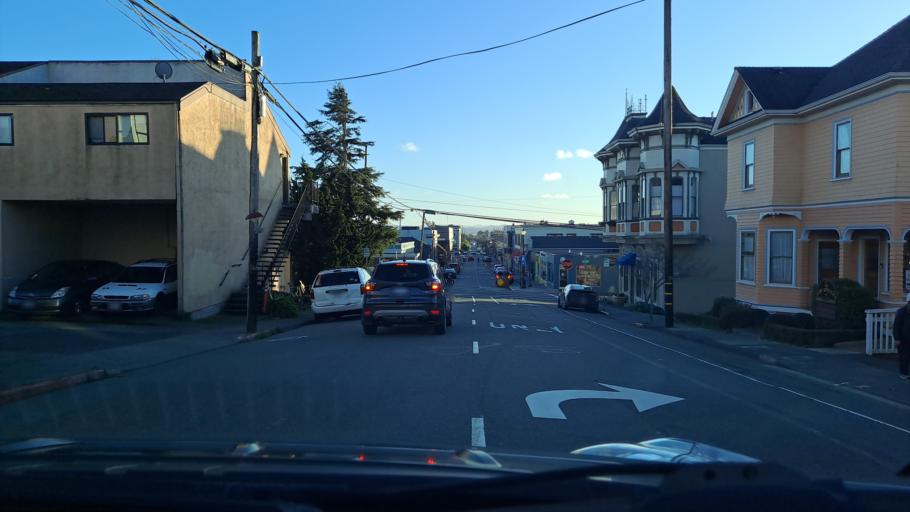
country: US
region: California
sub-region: Humboldt County
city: Arcata
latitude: 40.8711
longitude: -124.0860
